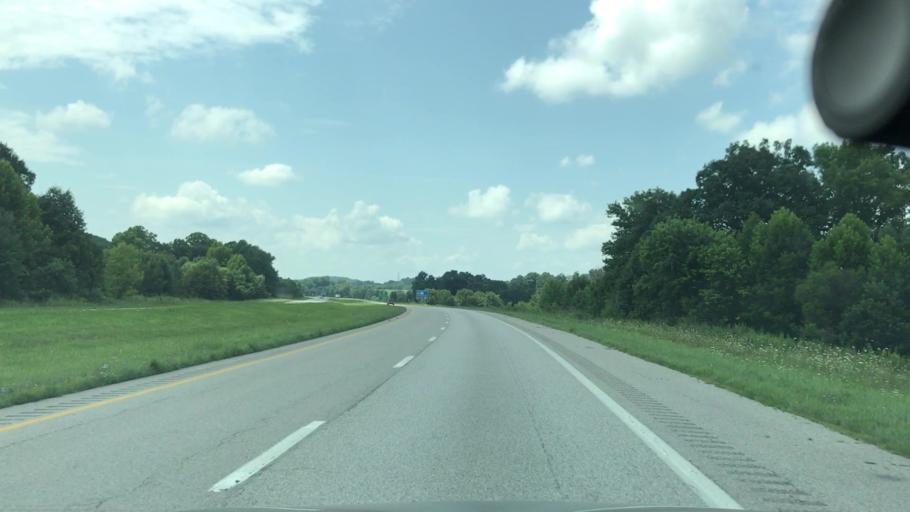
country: US
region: Ohio
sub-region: Gallia County
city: Gallipolis
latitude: 38.8937
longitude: -82.3637
